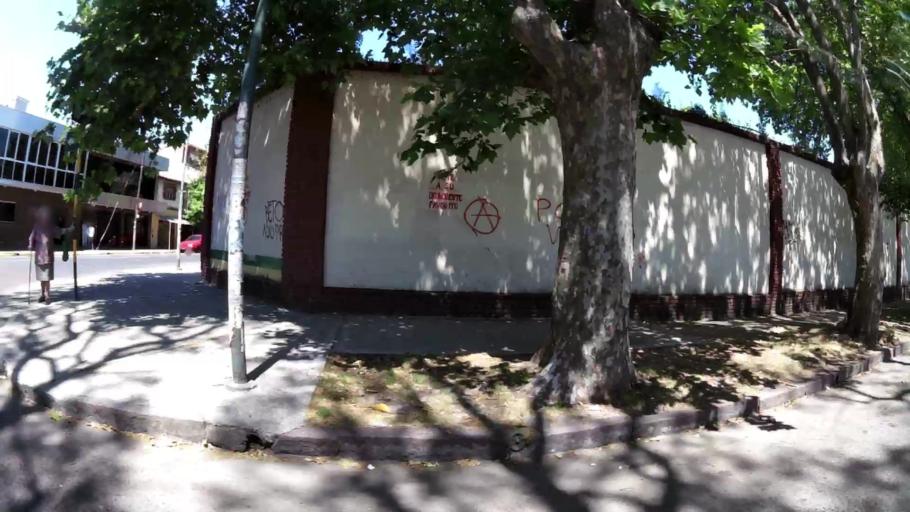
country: AR
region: Buenos Aires
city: Caseros
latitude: -34.5852
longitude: -58.5495
